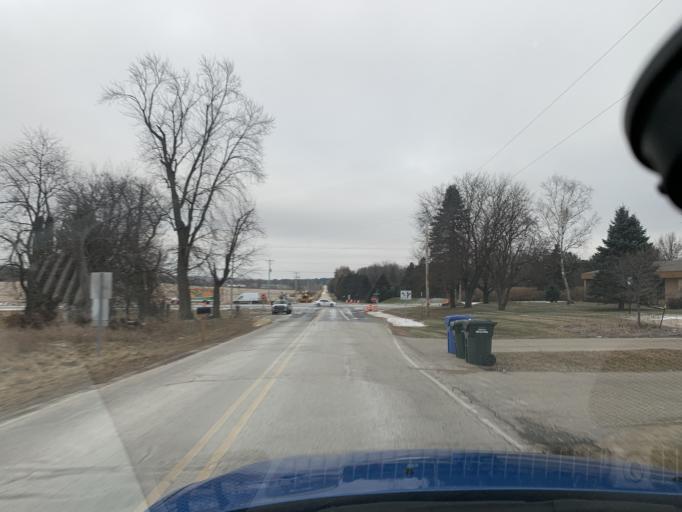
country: US
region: Wisconsin
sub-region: Dane County
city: Middleton
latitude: 43.0613
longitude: -89.5716
